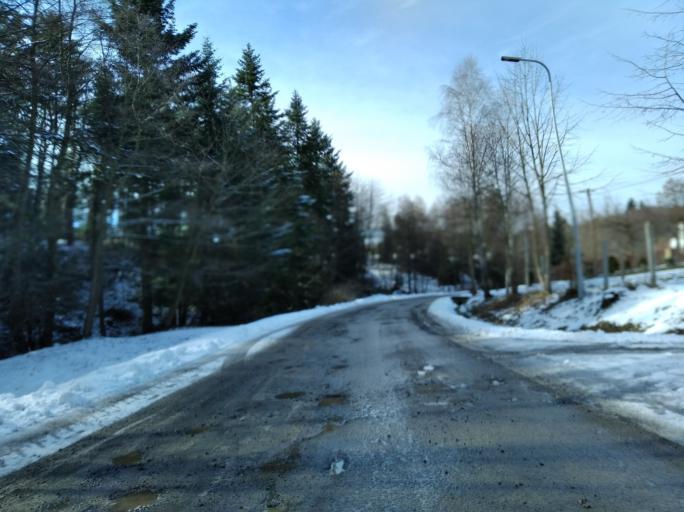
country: PL
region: Subcarpathian Voivodeship
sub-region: Powiat krosnienski
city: Korczyna
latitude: 49.7451
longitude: 21.8071
